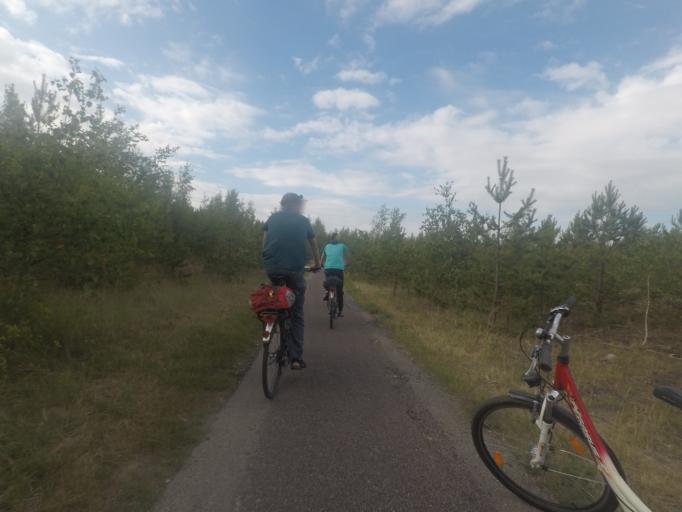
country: LT
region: Klaipedos apskritis
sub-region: Klaipeda
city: Klaipeda
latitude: 55.6382
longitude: 21.1167
